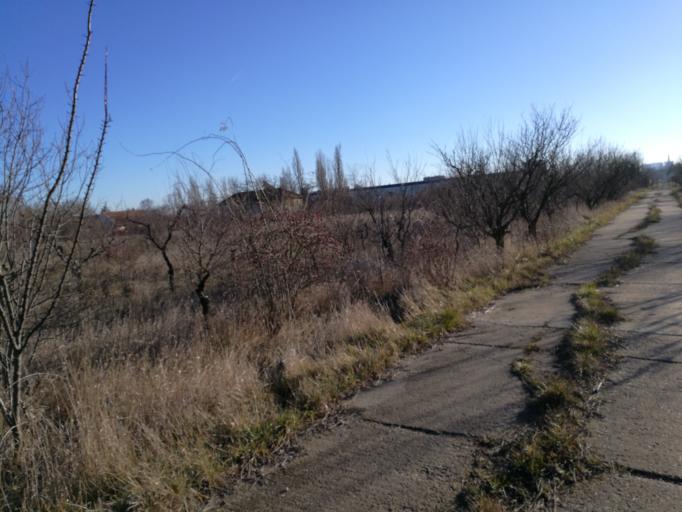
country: RO
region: Ilfov
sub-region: Comuna Otopeni
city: Otopeni
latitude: 44.5054
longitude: 26.0777
